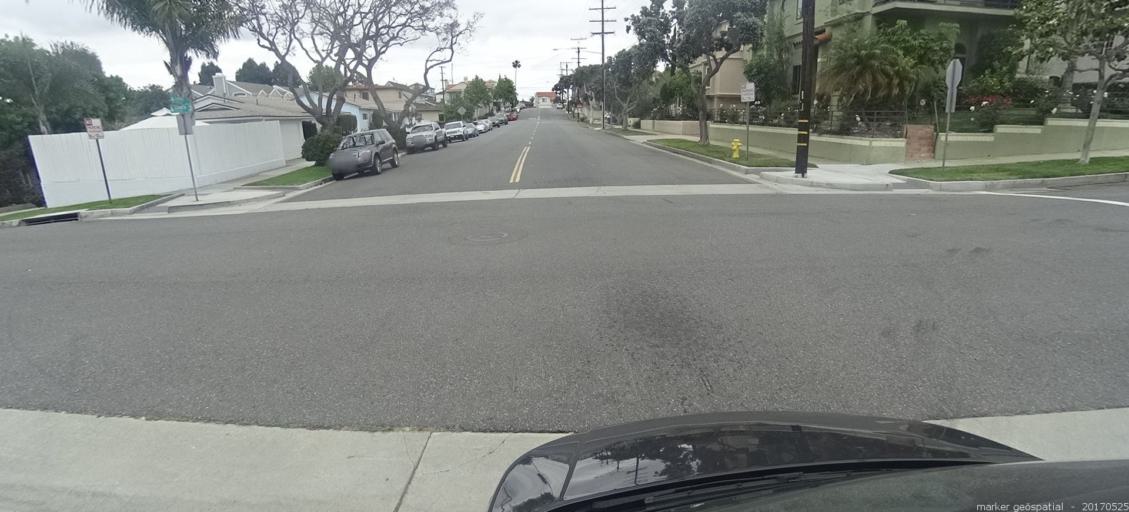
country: US
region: California
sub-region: Los Angeles County
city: Redondo Beach
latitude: 33.8405
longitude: -118.3791
